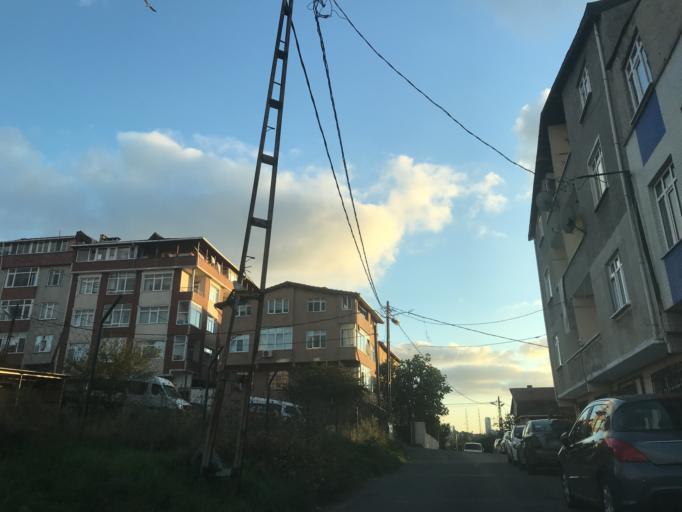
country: TR
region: Istanbul
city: Sisli
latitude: 41.1286
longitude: 29.0420
